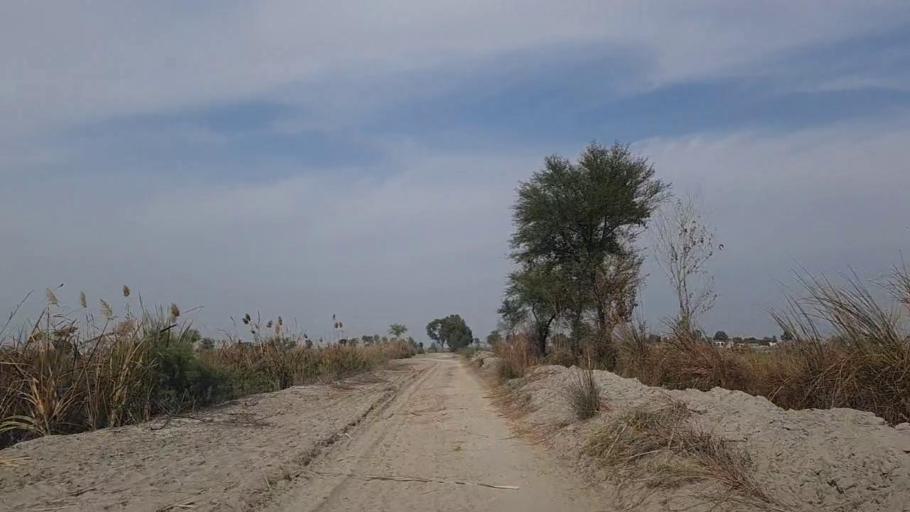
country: PK
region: Sindh
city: Daur
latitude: 26.4633
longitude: 68.4072
